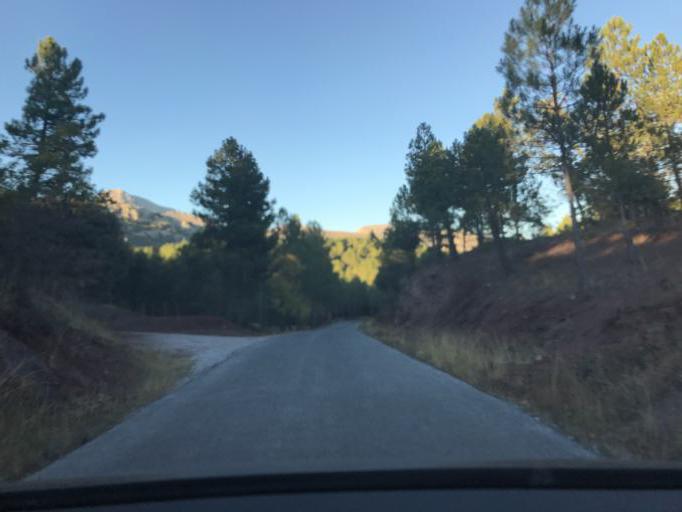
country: ES
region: Andalusia
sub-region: Provincia de Granada
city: Beas de Granada
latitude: 37.2987
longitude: -3.4719
